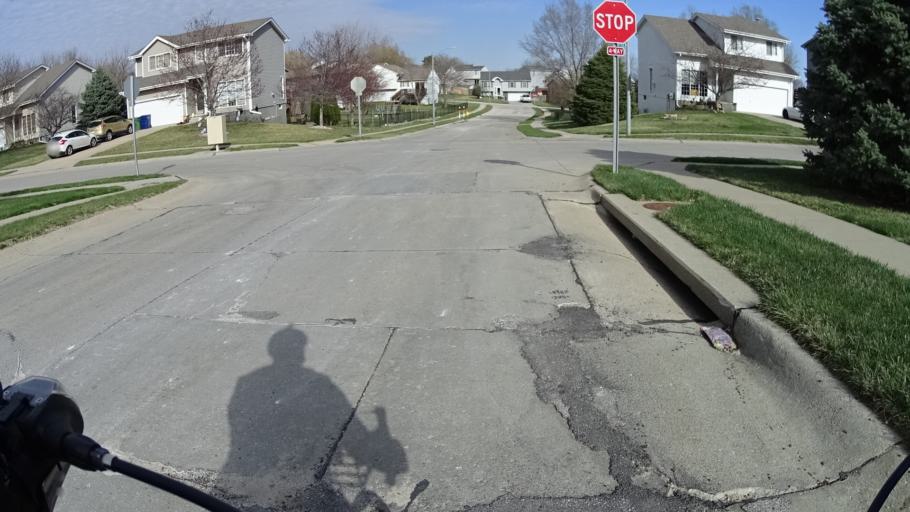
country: US
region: Nebraska
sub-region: Sarpy County
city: Offutt Air Force Base
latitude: 41.1098
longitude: -95.9614
